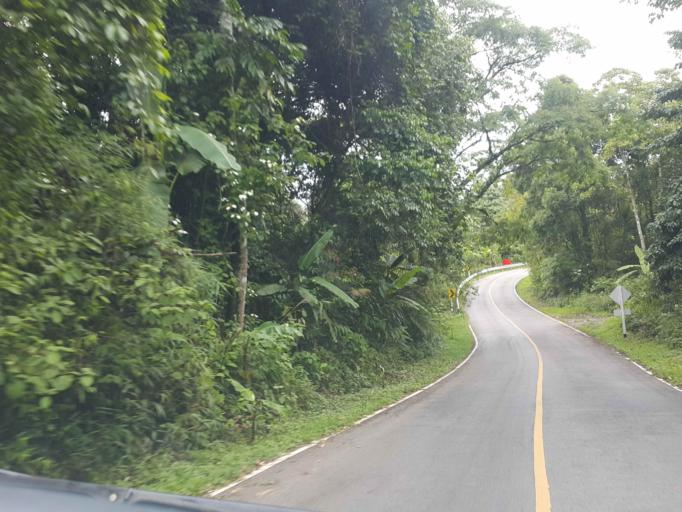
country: TH
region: Chiang Mai
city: Mae Chaem
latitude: 18.5228
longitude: 98.4833
